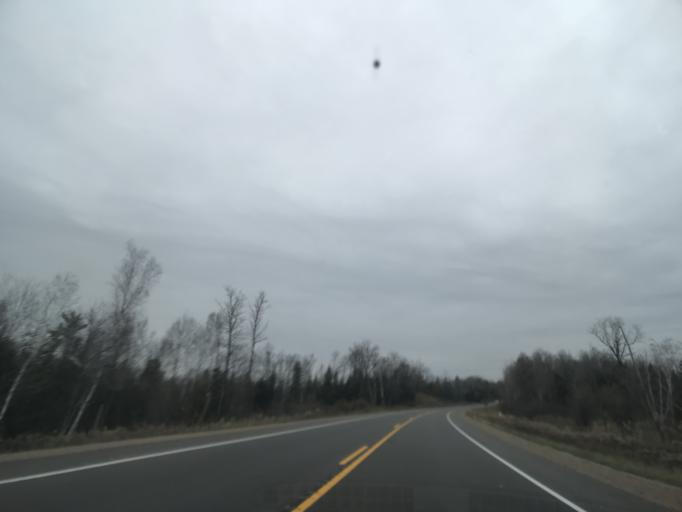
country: US
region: Wisconsin
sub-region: Menominee County
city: Legend Lake
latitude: 45.2629
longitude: -88.5133
